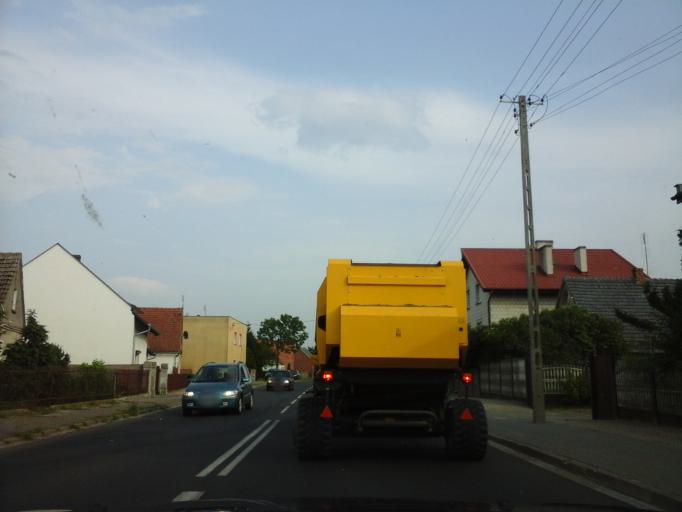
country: PL
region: Greater Poland Voivodeship
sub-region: Powiat koscianski
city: Koscian
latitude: 52.1017
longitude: 16.6400
